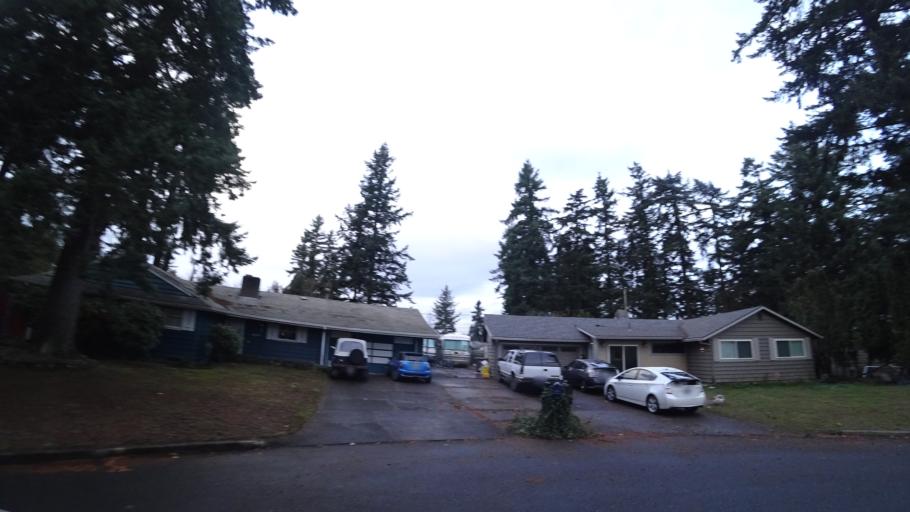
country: US
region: Oregon
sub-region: Multnomah County
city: Lents
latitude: 45.5304
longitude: -122.5363
